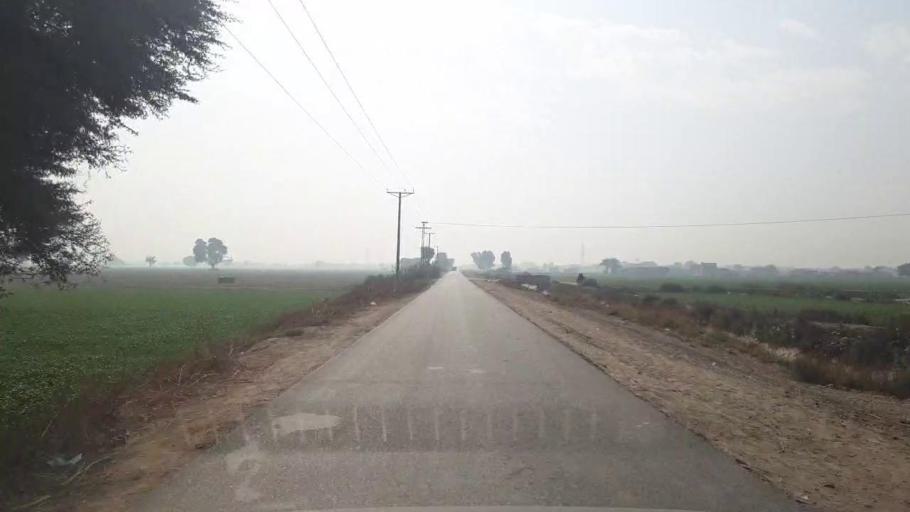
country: PK
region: Sindh
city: Hala
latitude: 25.8064
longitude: 68.4359
